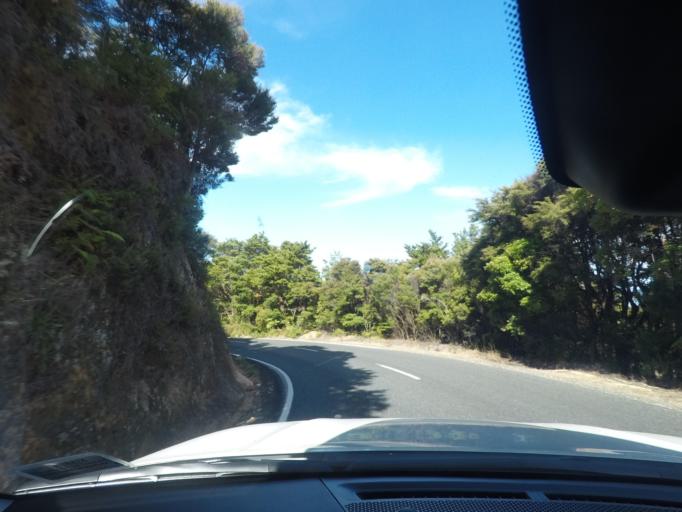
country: NZ
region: Northland
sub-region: Whangarei
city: Ngunguru
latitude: -35.6665
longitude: 174.4732
